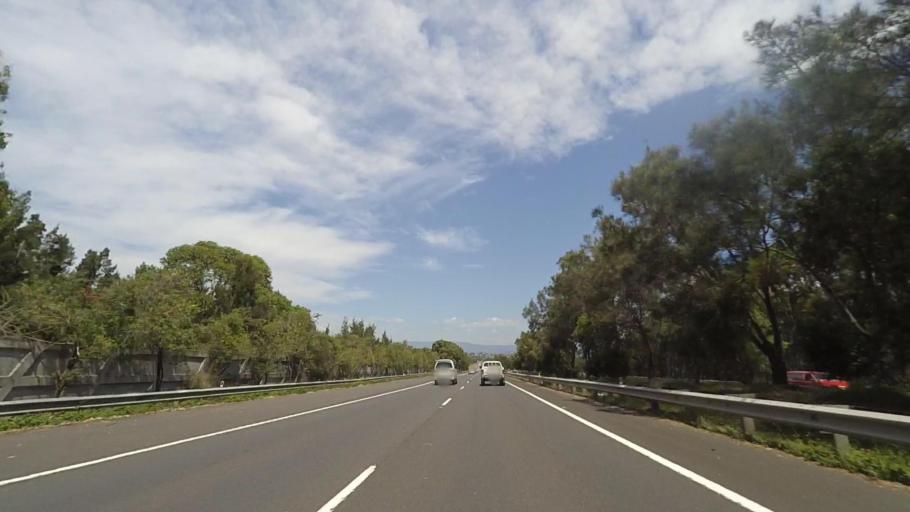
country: AU
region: New South Wales
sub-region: Wollongong
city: Berkeley
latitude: -34.4729
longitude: 150.8330
